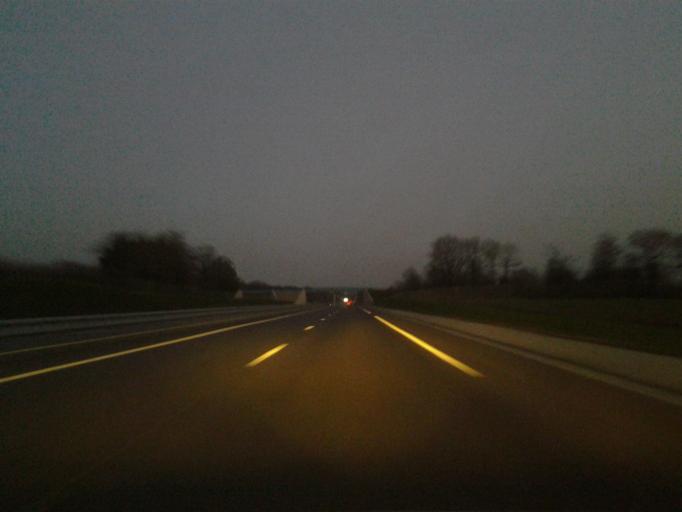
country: FR
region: Pays de la Loire
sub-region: Departement de la Vendee
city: Saint-Christophe-du-Ligneron
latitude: 46.8288
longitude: -1.8036
